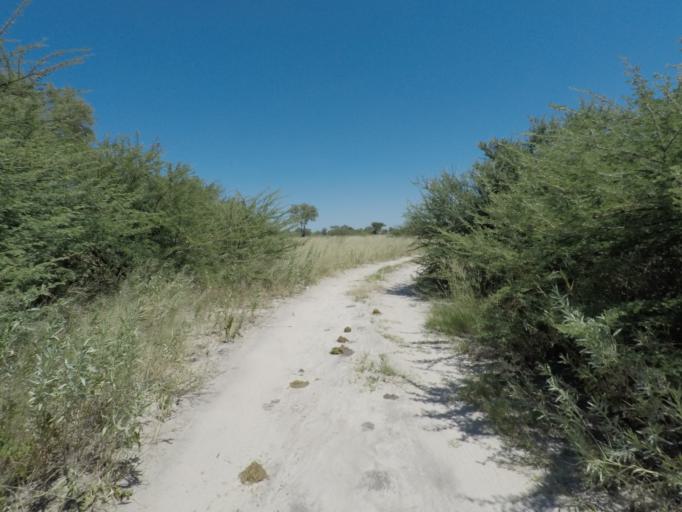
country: BW
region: North West
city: Maun
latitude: -19.4459
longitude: 23.5584
